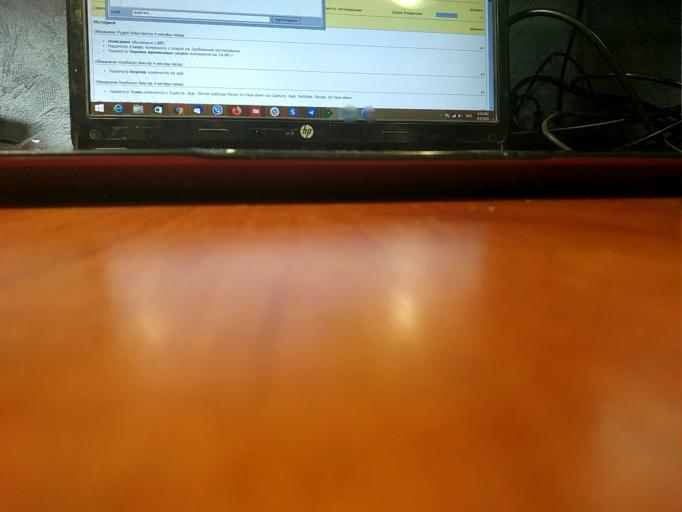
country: RU
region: Vologda
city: Ustyuzhna
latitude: 58.6641
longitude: 36.4250
